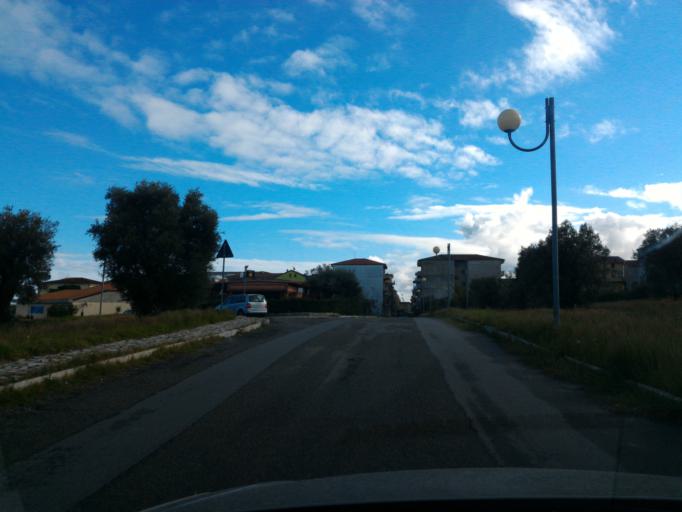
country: IT
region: Calabria
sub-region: Provincia di Crotone
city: Torretta
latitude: 39.4556
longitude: 17.0357
